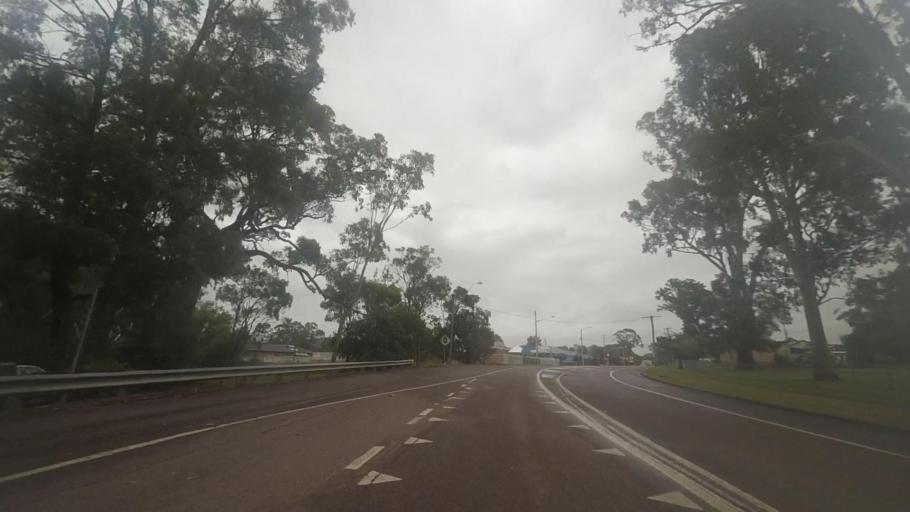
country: AU
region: New South Wales
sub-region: Port Stephens Shire
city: Port Stephens
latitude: -32.6547
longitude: 151.9674
